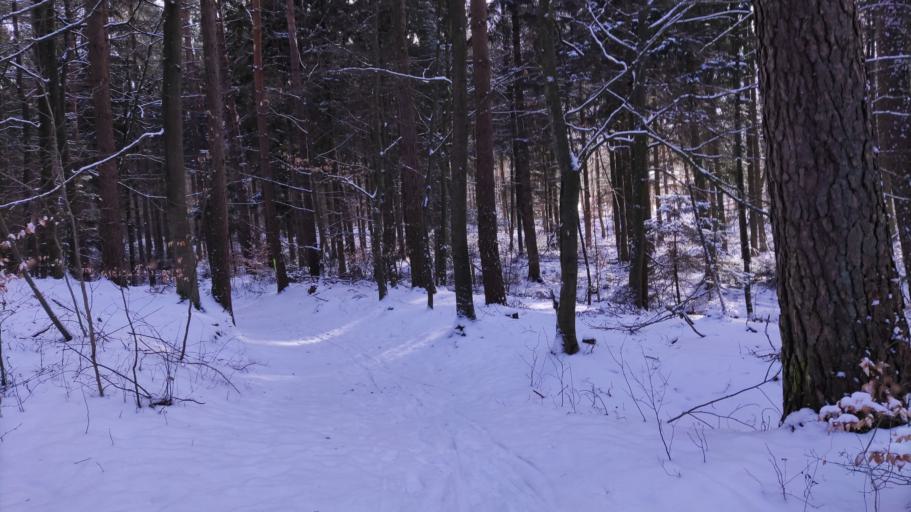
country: DE
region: Lower Saxony
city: Deutsch Evern
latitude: 53.2277
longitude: 10.4301
